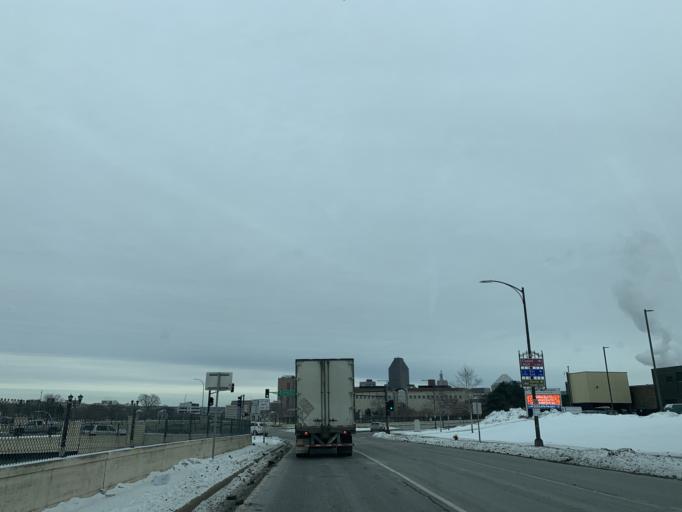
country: US
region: Minnesota
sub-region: Ramsey County
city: Saint Paul
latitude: 44.9503
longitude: -93.1107
